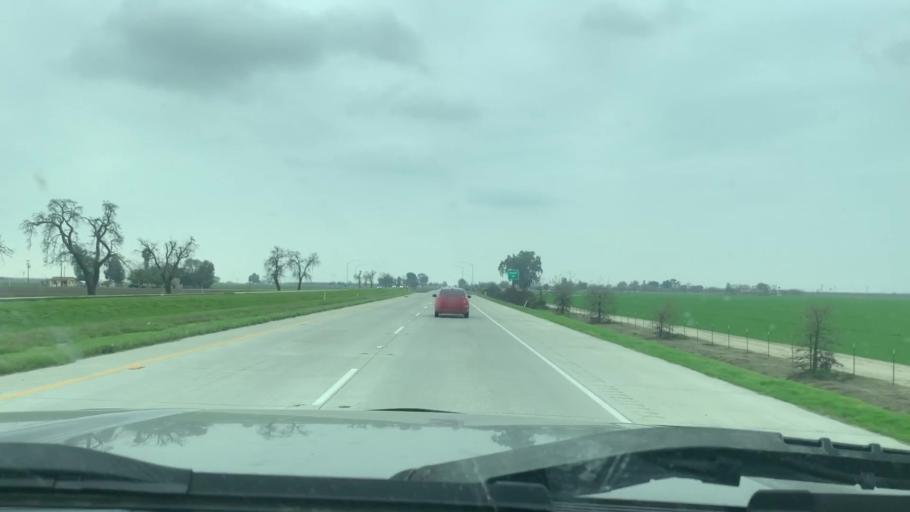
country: US
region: California
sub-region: Tulare County
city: Goshen
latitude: 36.3279
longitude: -119.4626
